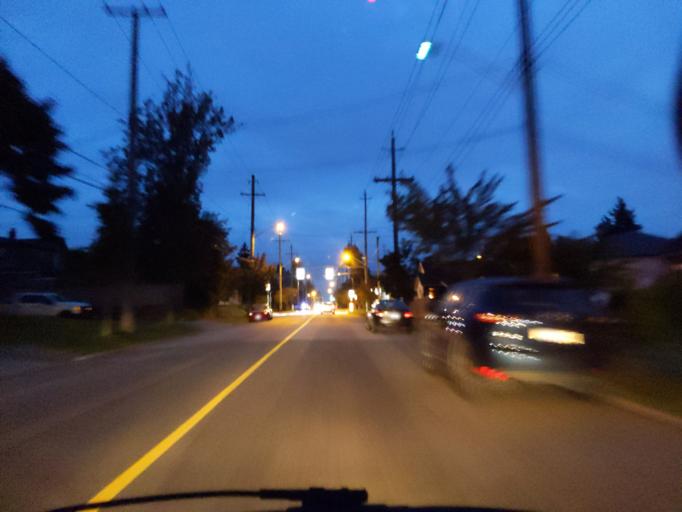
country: CA
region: British Columbia
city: New Westminster
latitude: 49.2179
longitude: -122.9205
